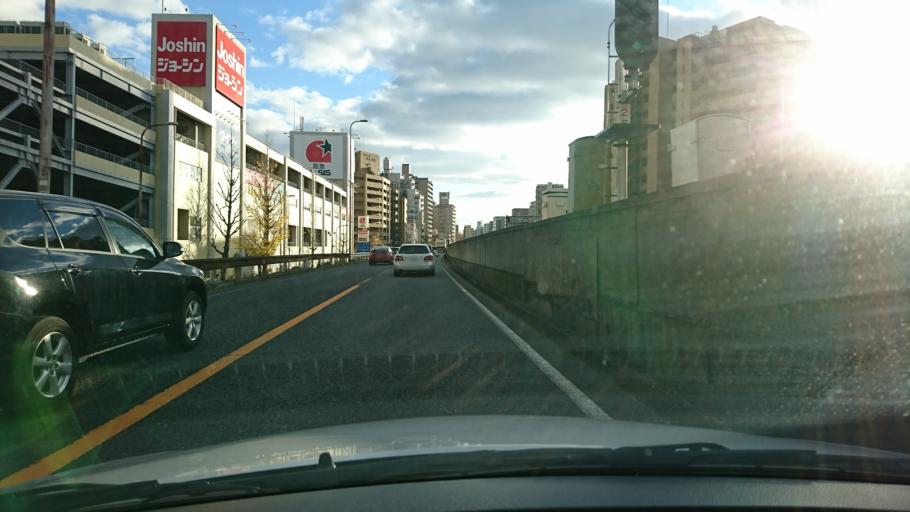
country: JP
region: Osaka
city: Suita
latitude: 34.7804
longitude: 135.4971
